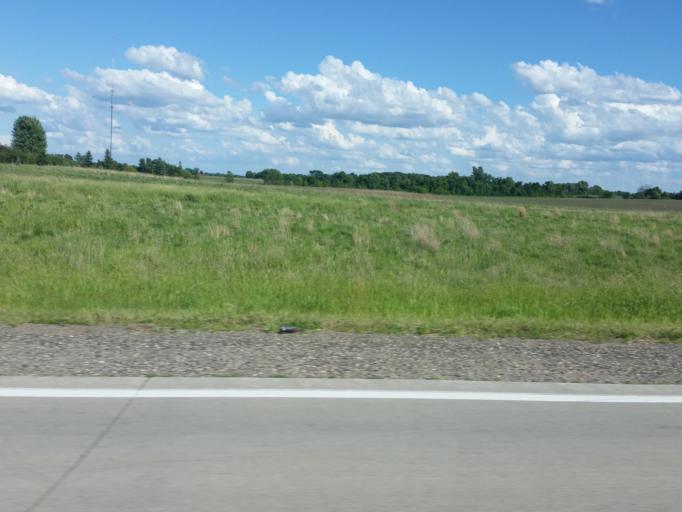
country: US
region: Minnesota
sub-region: McLeod County
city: Winsted
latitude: 44.9204
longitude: -94.1844
